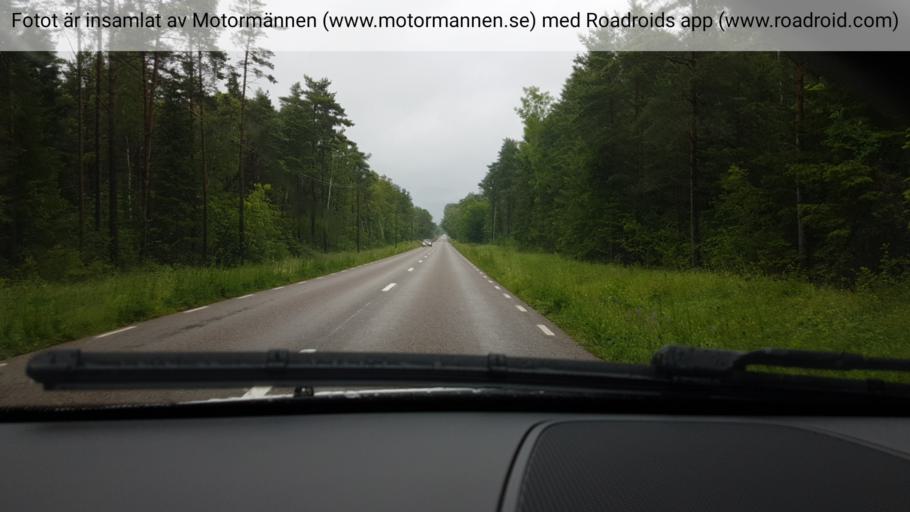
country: SE
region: Gotland
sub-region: Gotland
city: Slite
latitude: 57.6391
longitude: 18.7653
